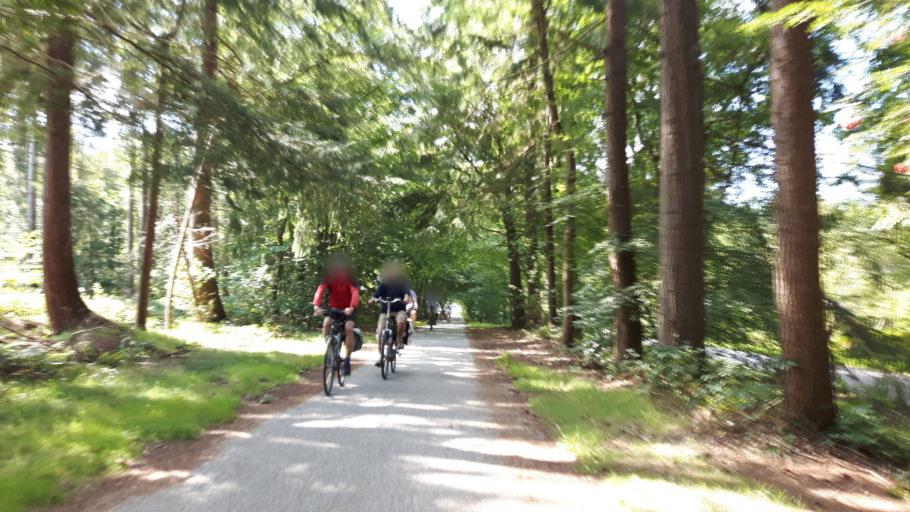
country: NL
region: Friesland
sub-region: Gemeente Smallingerland
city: Drachtstercompagnie
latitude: 53.0775
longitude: 6.2493
